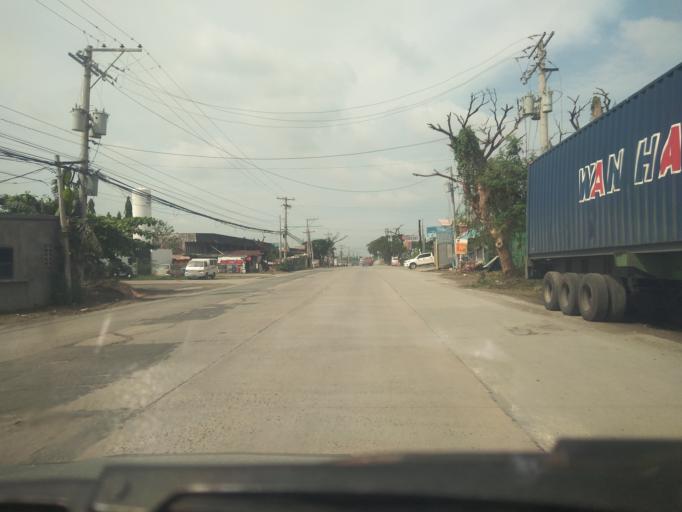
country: PH
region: Central Luzon
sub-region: Province of Pampanga
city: Santo Domingo
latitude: 15.0032
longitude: 120.7223
